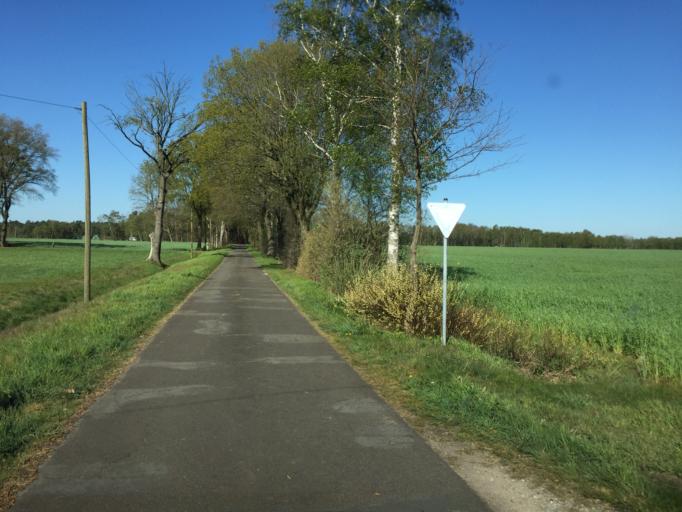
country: DE
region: Lower Saxony
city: Wehrbleck
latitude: 52.5684
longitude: 8.6913
